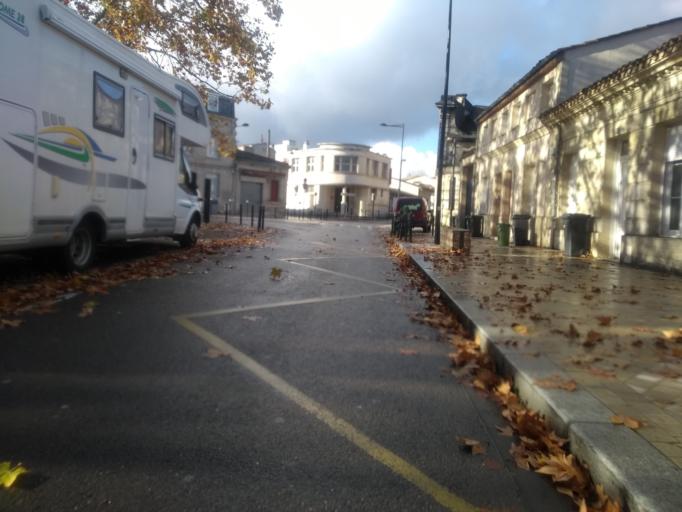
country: FR
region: Aquitaine
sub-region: Departement de la Gironde
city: Begles
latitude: 44.8244
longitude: -0.5511
